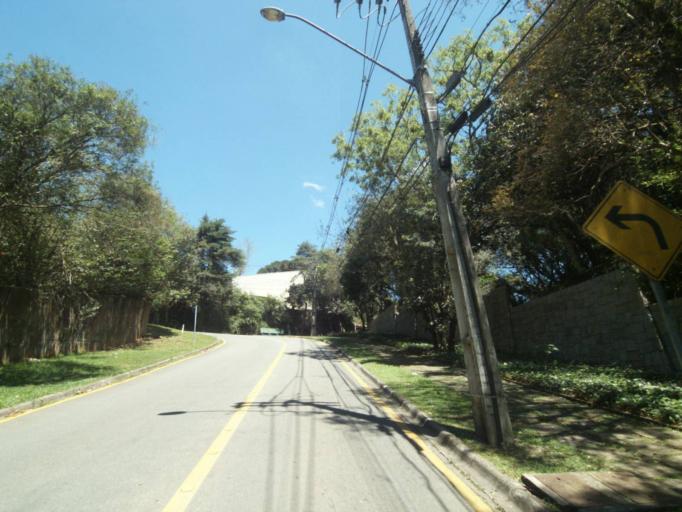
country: BR
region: Parana
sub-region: Curitiba
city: Curitiba
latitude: -25.3806
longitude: -49.2687
